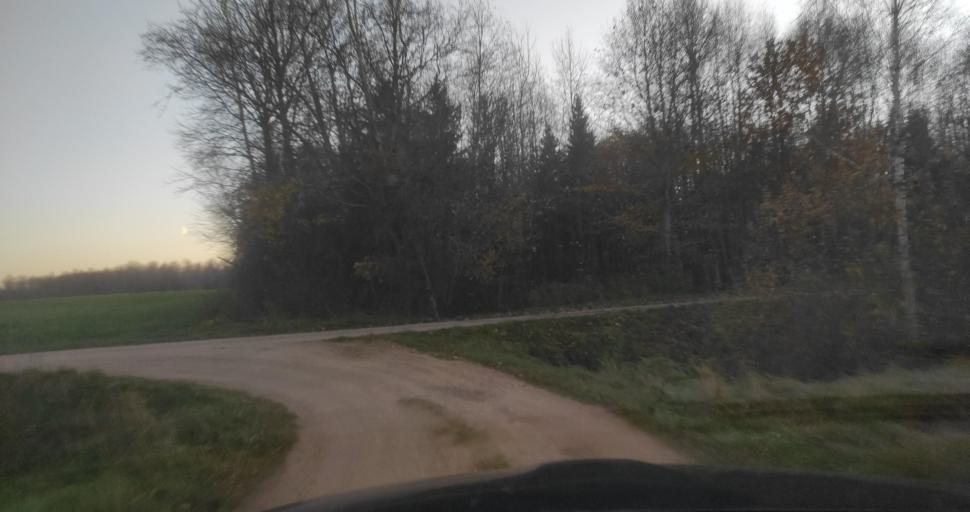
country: LV
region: Saldus Rajons
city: Saldus
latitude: 56.8035
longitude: 22.2751
